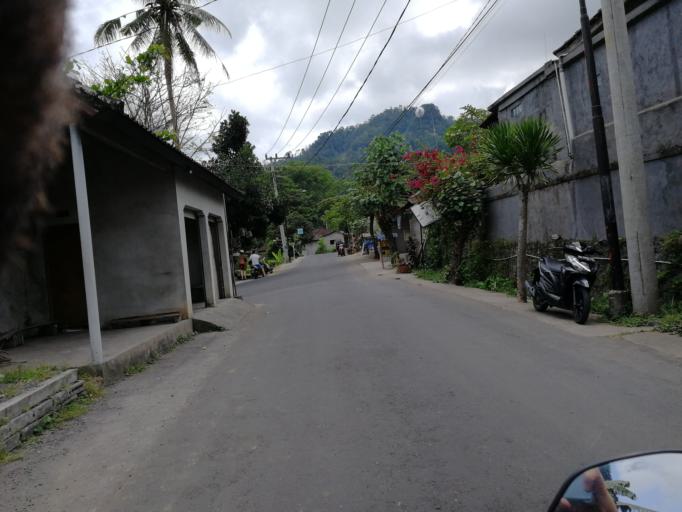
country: ID
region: Bali
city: Banjar Wangsian
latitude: -8.4681
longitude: 115.4449
